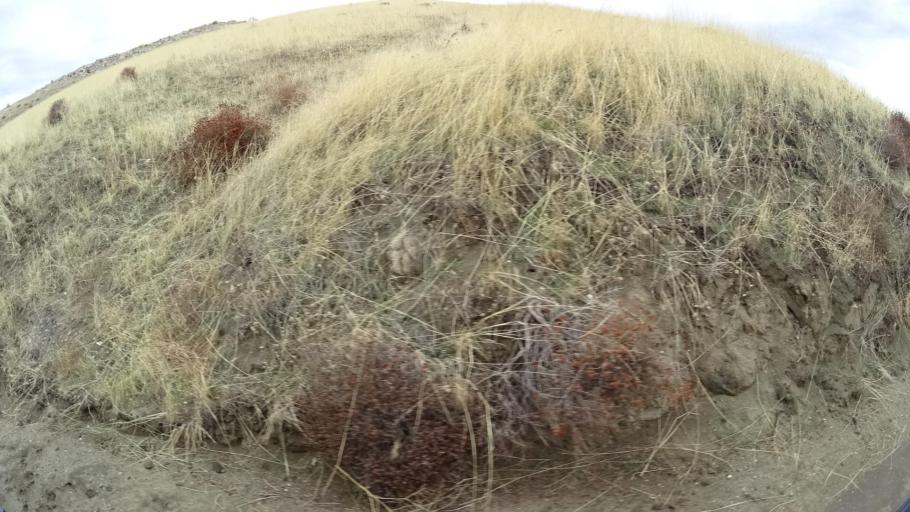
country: US
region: California
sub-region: Kern County
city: Arvin
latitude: 35.1269
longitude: -118.7582
